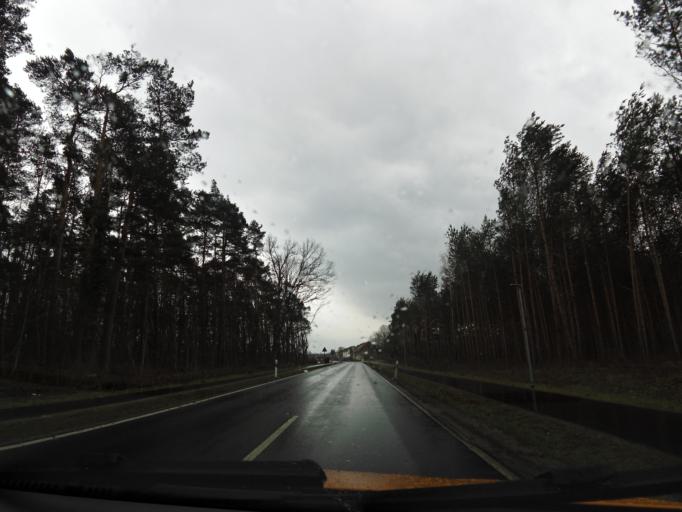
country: DE
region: Brandenburg
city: Rangsdorf
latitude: 52.3422
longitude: 13.4003
